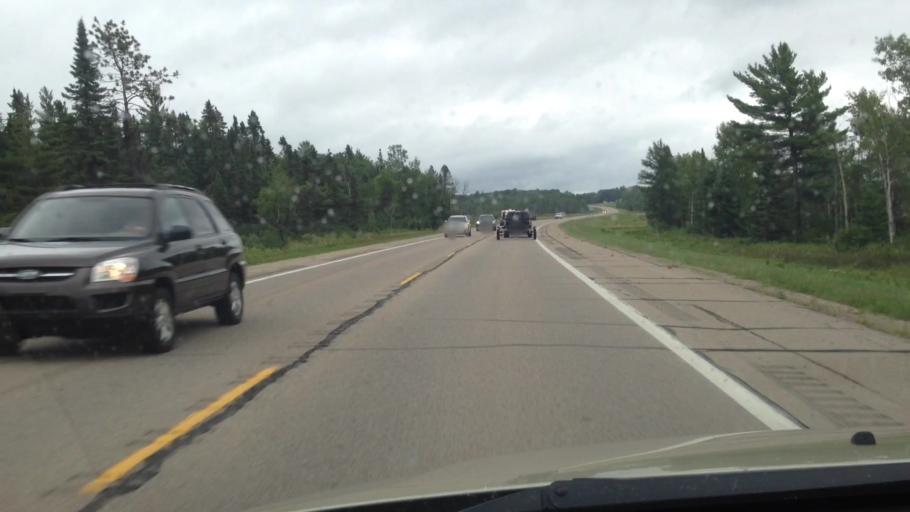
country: US
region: Michigan
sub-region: Delta County
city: Gladstone
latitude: 45.8991
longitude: -86.7639
